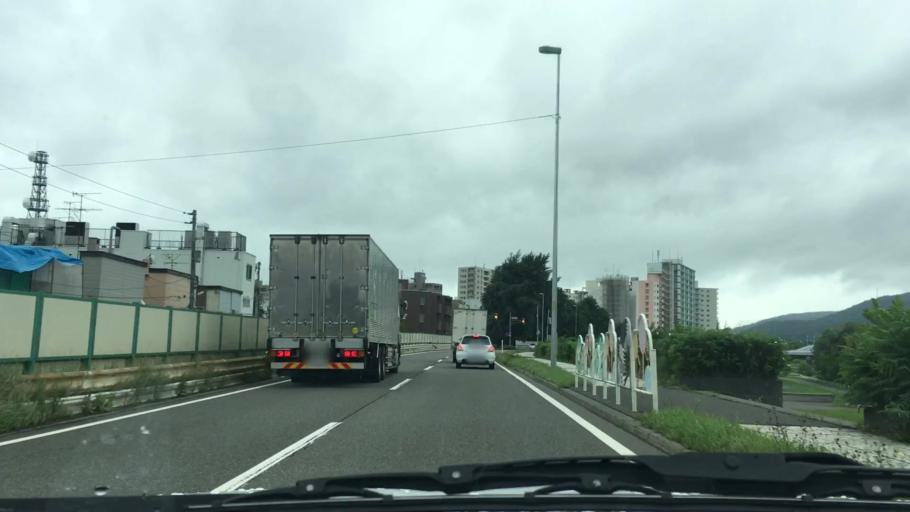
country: JP
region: Hokkaido
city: Sapporo
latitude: 43.0429
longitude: 141.3609
